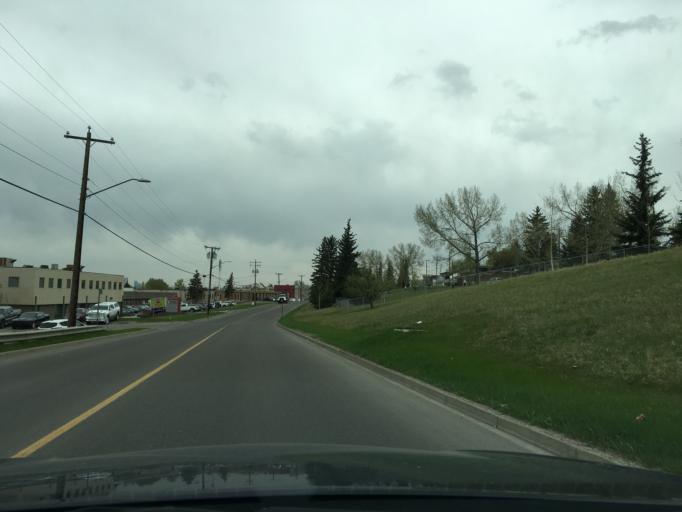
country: CA
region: Alberta
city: Calgary
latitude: 50.9845
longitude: -114.0683
